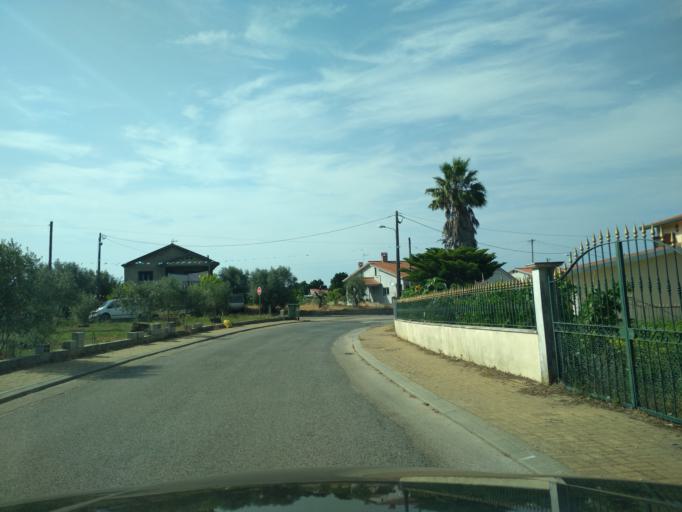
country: PT
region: Aveiro
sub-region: Mealhada
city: Mealhada
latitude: 40.3725
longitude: -8.5053
